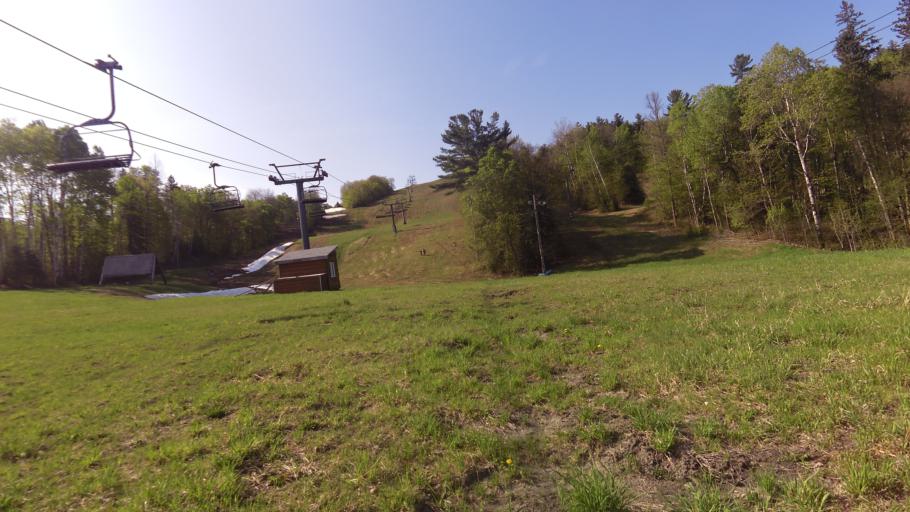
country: CA
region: Quebec
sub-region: Outaouais
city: Wakefield
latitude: 45.6450
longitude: -75.8509
